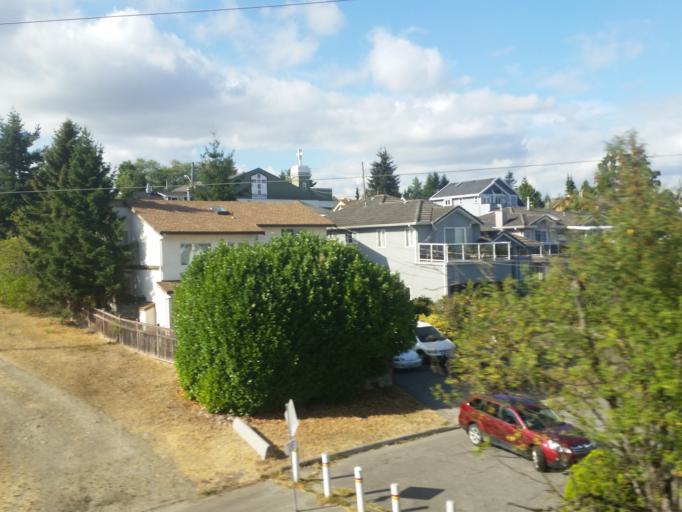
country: CA
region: British Columbia
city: New Westminster
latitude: 49.1994
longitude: -122.9522
